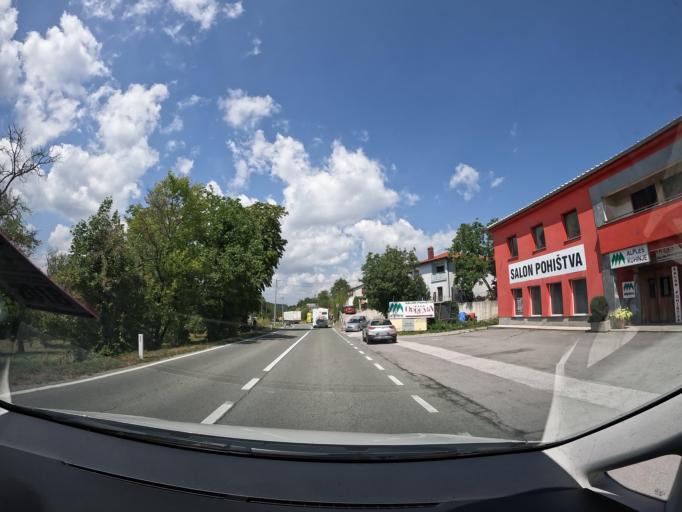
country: SI
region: Ilirska Bistrica
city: Ilirska Bistrica
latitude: 45.5004
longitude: 14.2713
